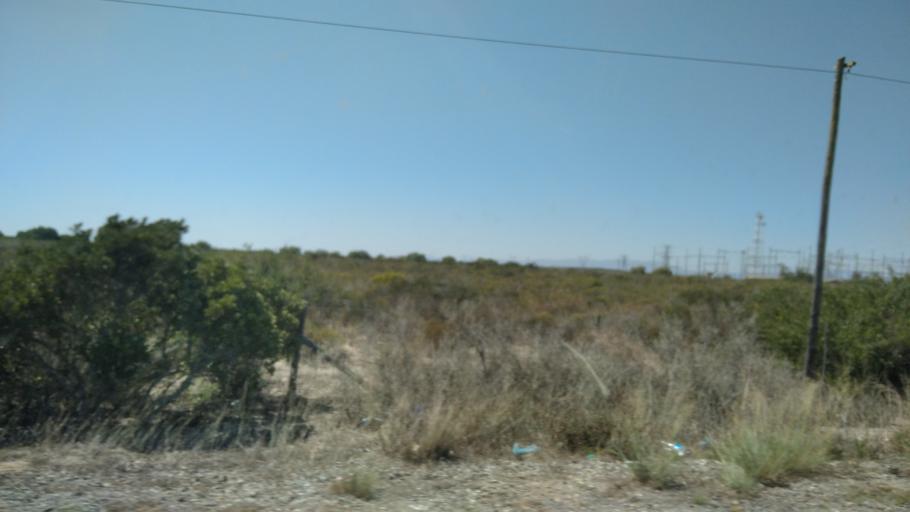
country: ZA
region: Western Cape
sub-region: West Coast District Municipality
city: Vredenburg
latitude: -33.0093
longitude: 18.2280
